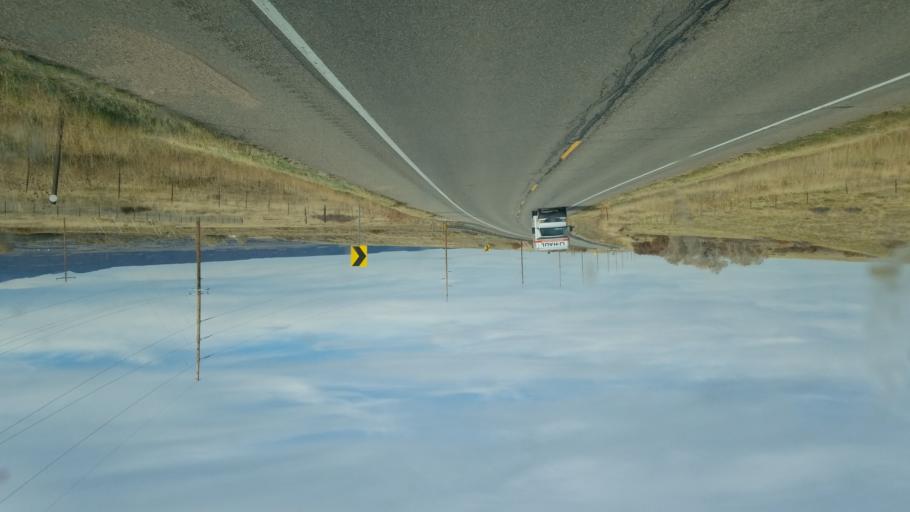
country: US
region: Colorado
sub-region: Huerfano County
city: Walsenburg
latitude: 37.5413
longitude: -105.0688
